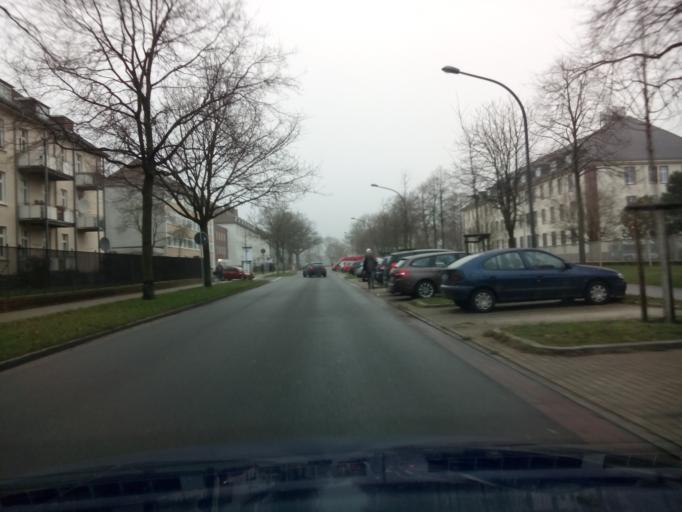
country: DE
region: Bremen
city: Bremen
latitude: 53.0545
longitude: 8.8229
